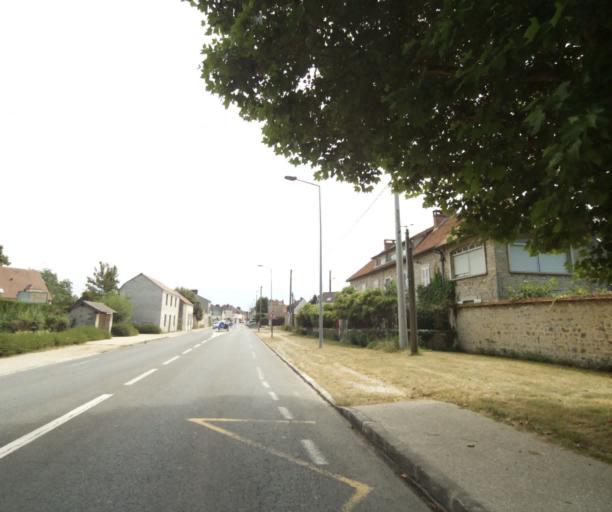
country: FR
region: Ile-de-France
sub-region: Departement de Seine-et-Marne
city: Chailly-en-Biere
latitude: 48.4685
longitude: 2.6052
